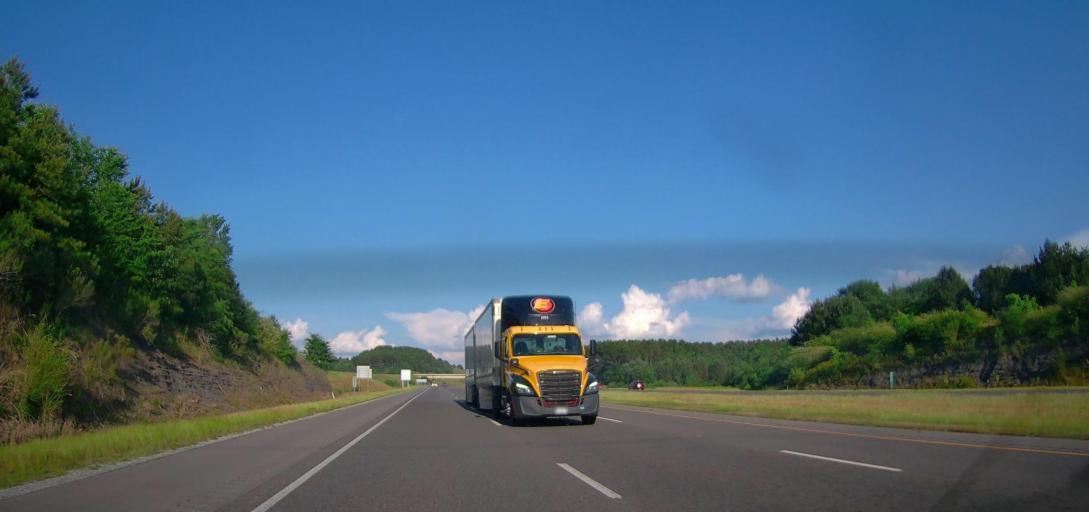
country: US
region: Alabama
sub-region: Walker County
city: Cordova
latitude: 33.7905
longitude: -87.2270
